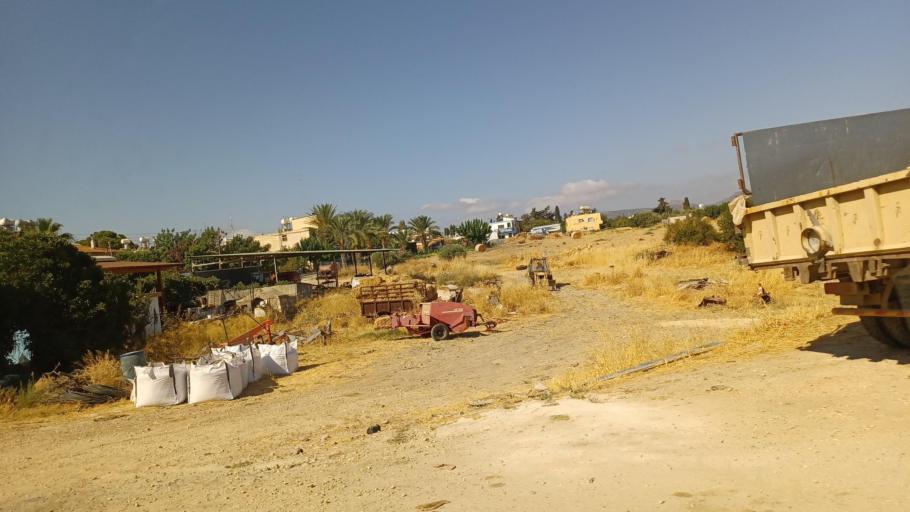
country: CY
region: Pafos
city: Polis
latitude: 35.0382
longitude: 32.4276
